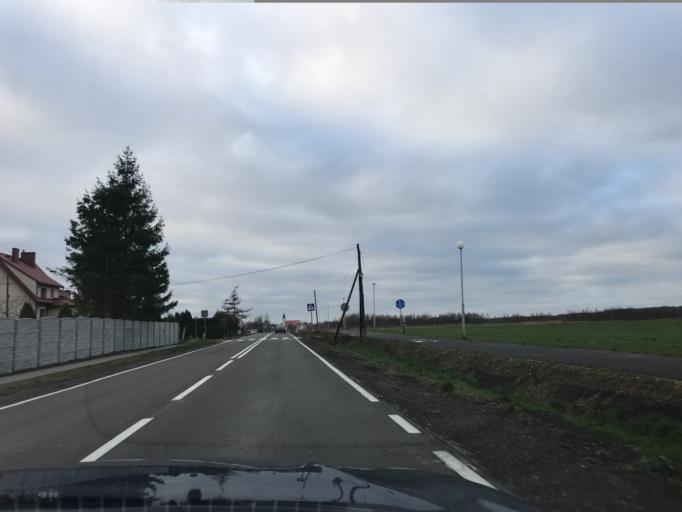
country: PL
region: West Pomeranian Voivodeship
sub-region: Powiat drawski
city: Zlocieniec
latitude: 53.5343
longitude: 16.0357
